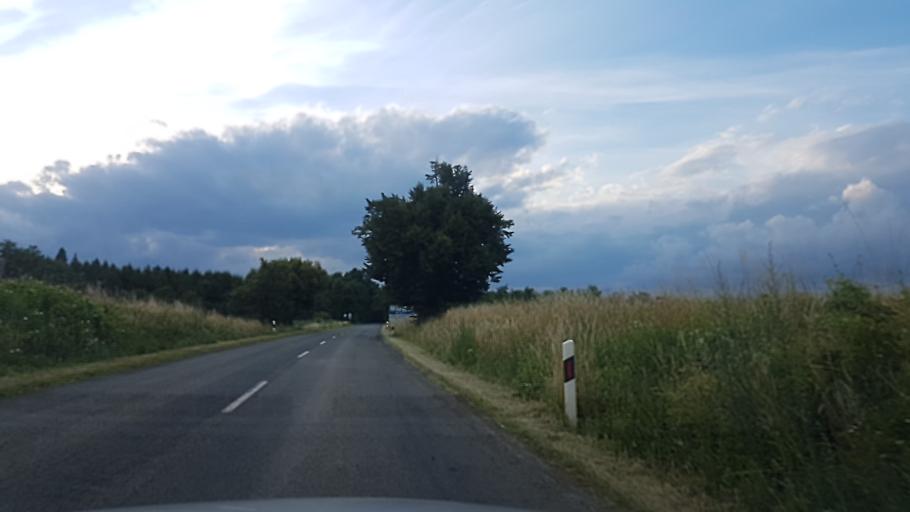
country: HU
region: Somogy
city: Kaposvar
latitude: 46.2581
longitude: 17.8305
